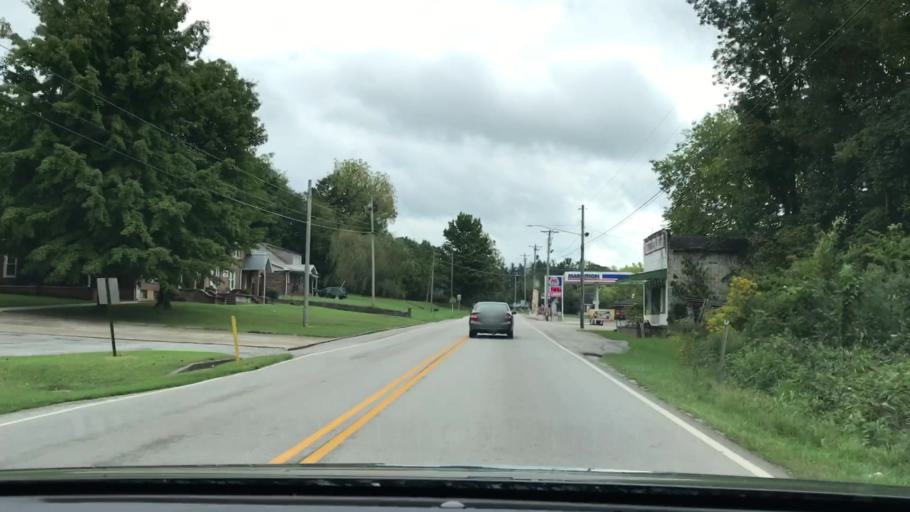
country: US
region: Kentucky
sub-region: Metcalfe County
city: Edmonton
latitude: 36.8859
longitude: -85.7074
